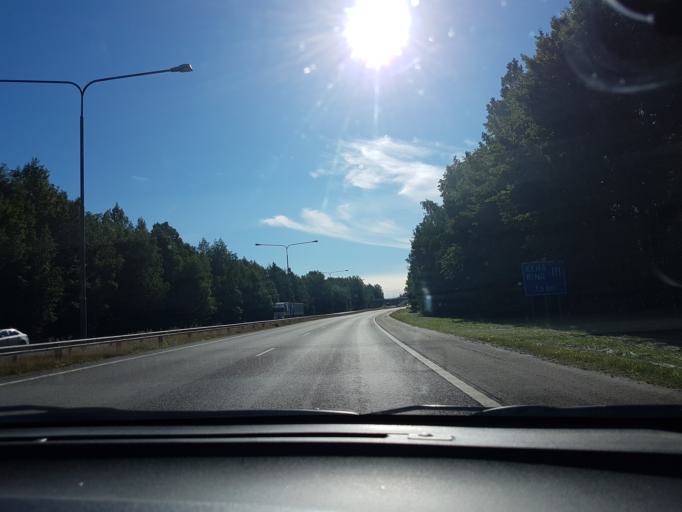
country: FI
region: Uusimaa
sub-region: Helsinki
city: Vantaa
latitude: 60.2541
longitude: 25.0919
